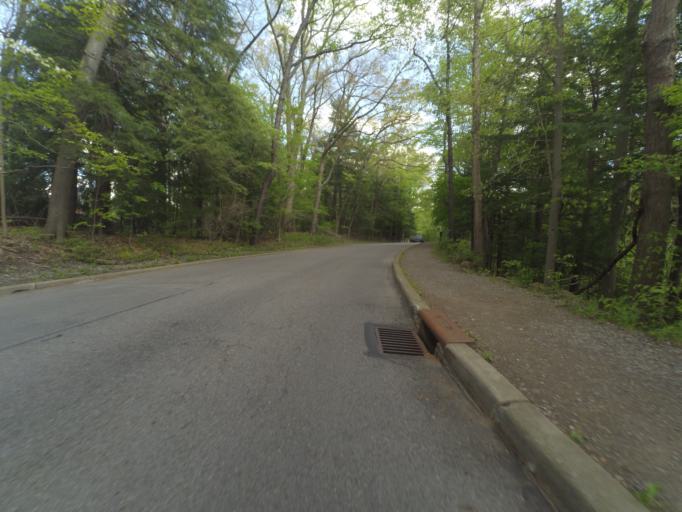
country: US
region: Ohio
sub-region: Mahoning County
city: Youngstown
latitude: 41.0685
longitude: -80.6846
